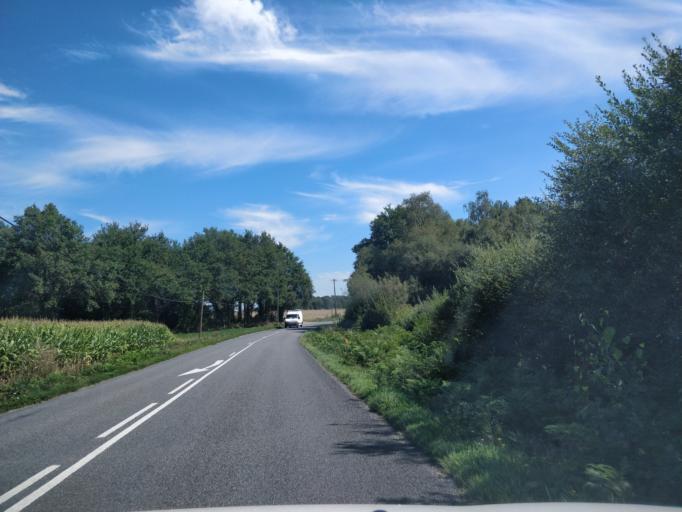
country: FR
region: Brittany
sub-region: Departement d'Ille-et-Vilaine
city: Grand-Fougeray
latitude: 47.6827
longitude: -1.7540
